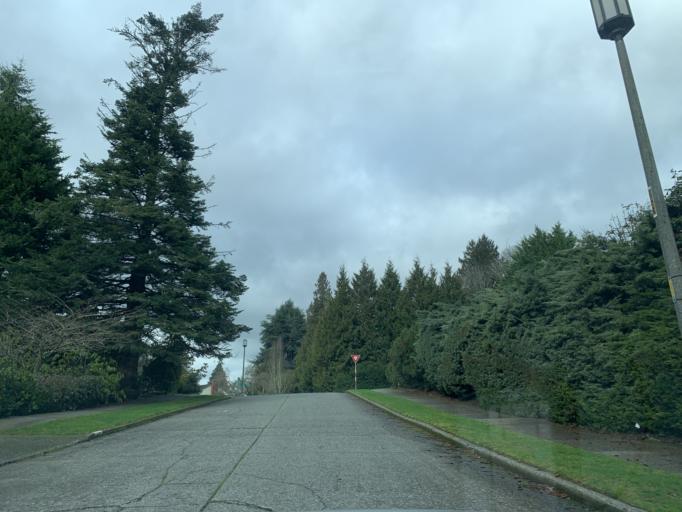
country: US
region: Washington
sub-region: King County
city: Yarrow Point
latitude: 47.6680
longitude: -122.2688
